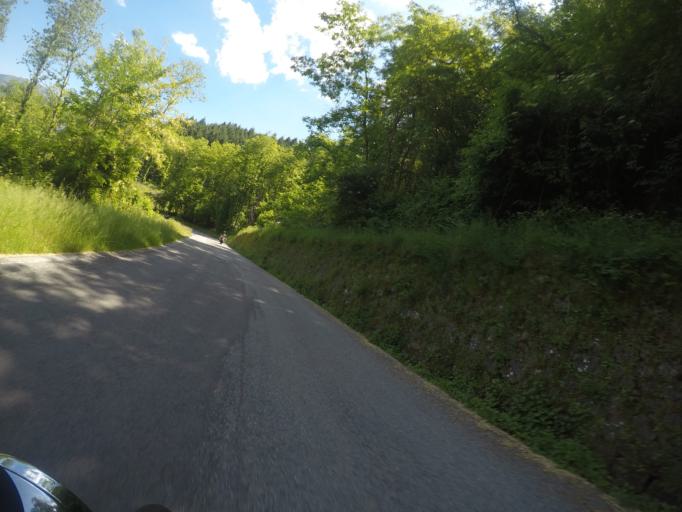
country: IT
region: Tuscany
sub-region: Provincia di Lucca
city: Careggine
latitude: 44.1355
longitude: 10.3448
